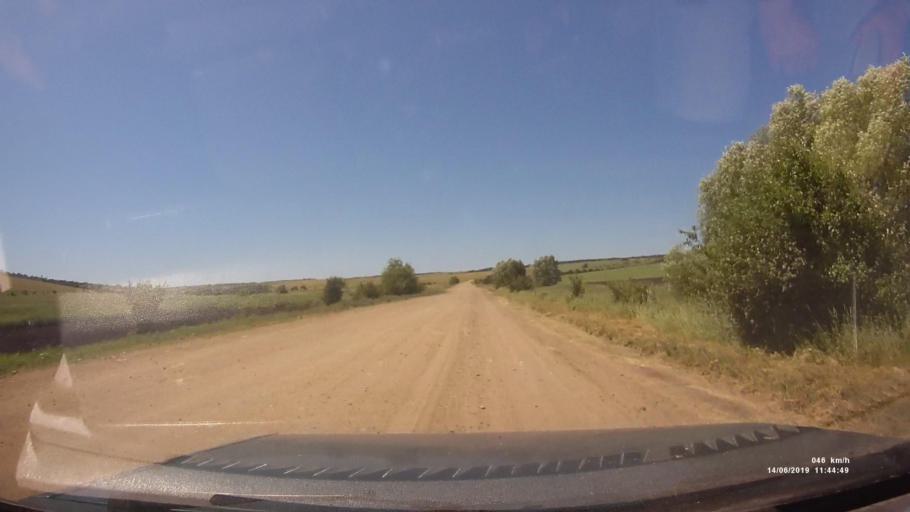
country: RU
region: Rostov
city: Kazanskaya
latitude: 49.8535
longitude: 41.3195
